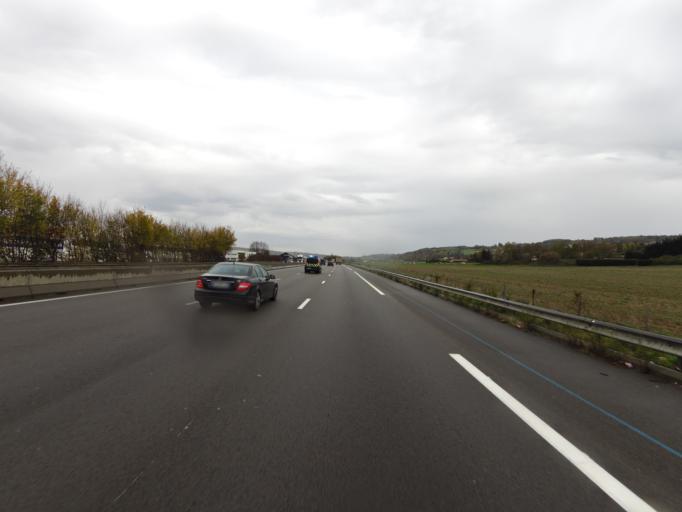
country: FR
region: Rhone-Alpes
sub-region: Departement de l'Isere
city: Reventin-Vaugris
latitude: 45.4623
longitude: 4.8327
